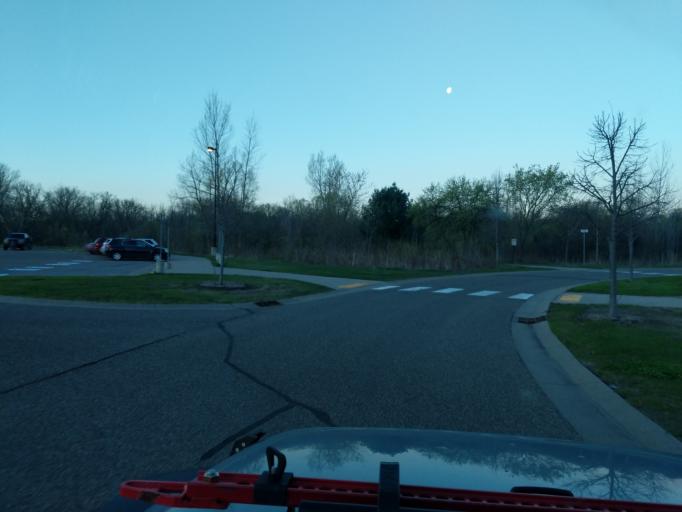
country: US
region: Wisconsin
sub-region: Pierce County
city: River Falls
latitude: 44.8504
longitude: -92.6145
